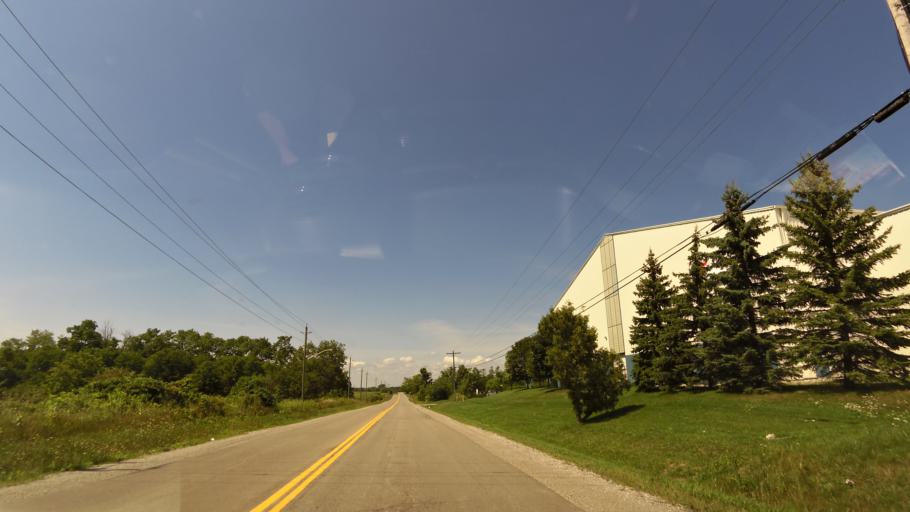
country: CA
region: Ontario
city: Ancaster
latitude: 43.1609
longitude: -79.9341
